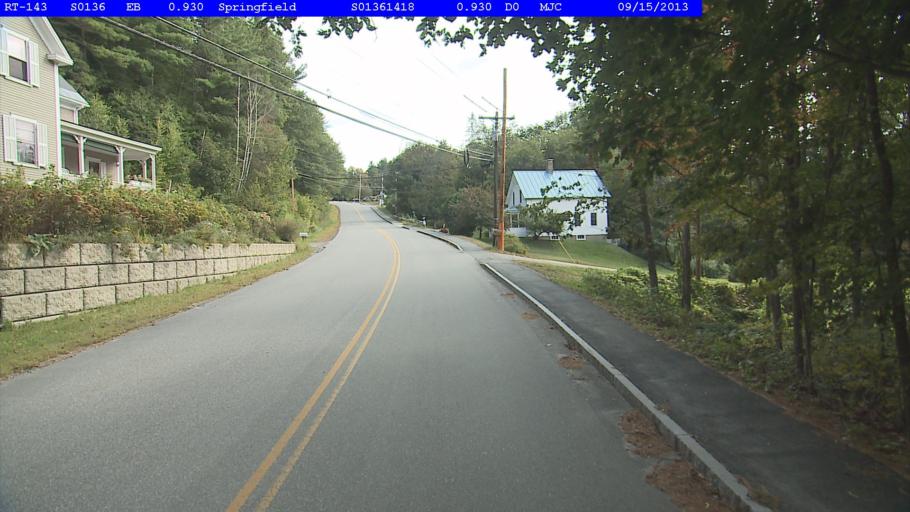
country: US
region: Vermont
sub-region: Windsor County
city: Springfield
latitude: 43.2939
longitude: -72.4678
